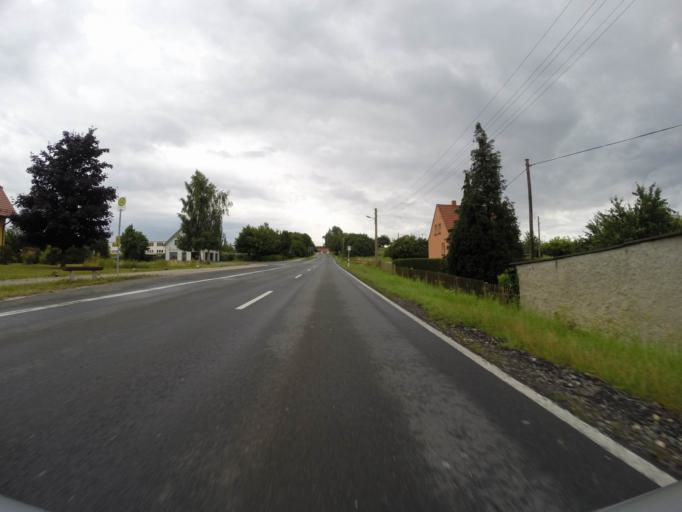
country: DE
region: Thuringia
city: Serba
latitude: 50.9526
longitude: 11.8178
